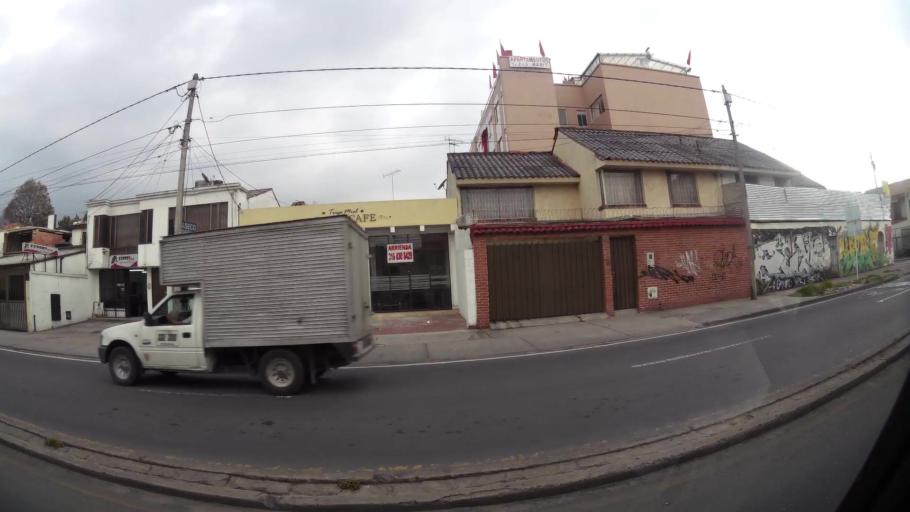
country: CO
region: Bogota D.C.
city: Barrio San Luis
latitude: 4.7187
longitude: -74.0704
